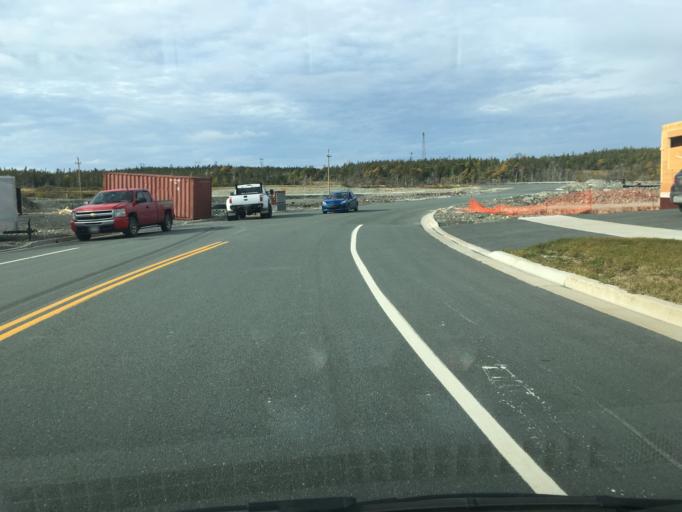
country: CA
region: Newfoundland and Labrador
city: Mount Pearl
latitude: 47.5569
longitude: -52.8029
